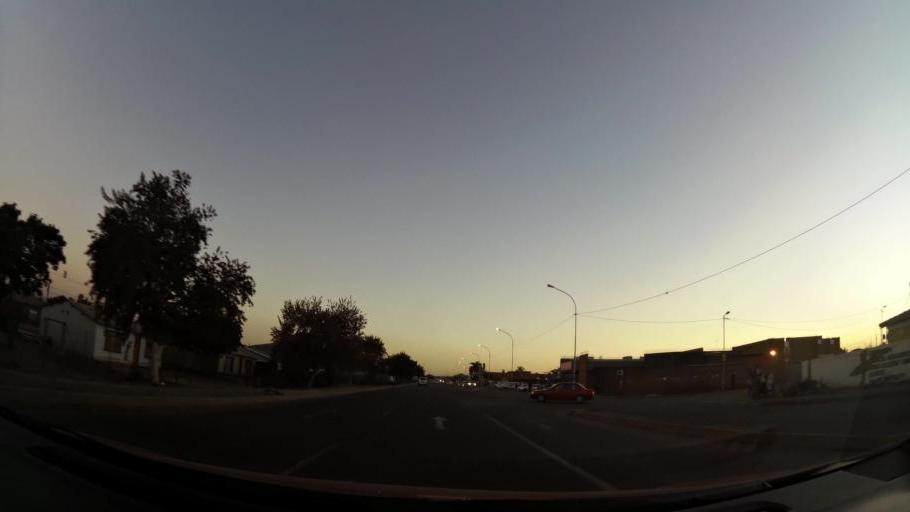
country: ZA
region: North-West
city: Ga-Rankuwa
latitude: -25.5926
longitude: 27.9815
